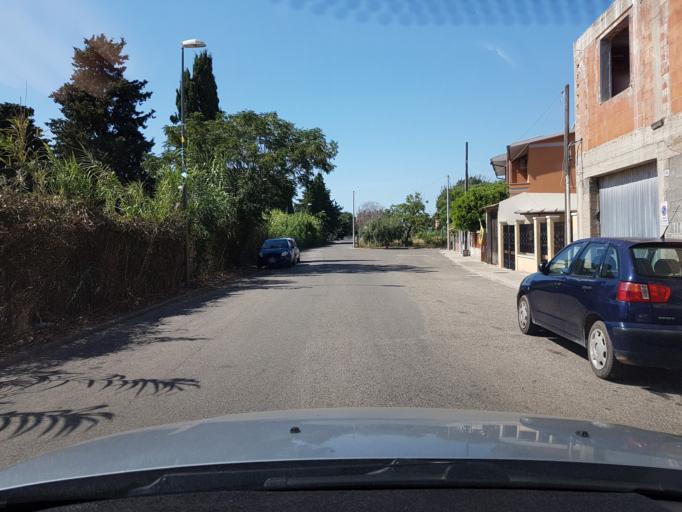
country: IT
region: Sardinia
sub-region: Provincia di Oristano
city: Donigala Fenugheddu
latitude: 39.9328
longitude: 8.5720
